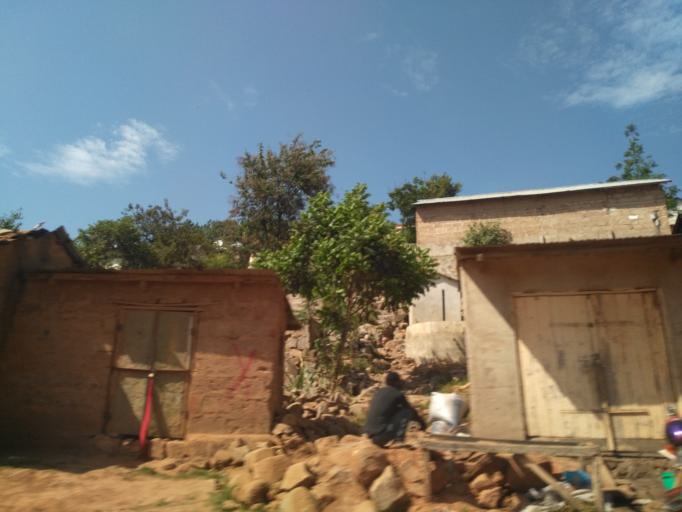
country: TZ
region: Mwanza
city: Mwanza
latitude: -2.4905
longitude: 32.8951
